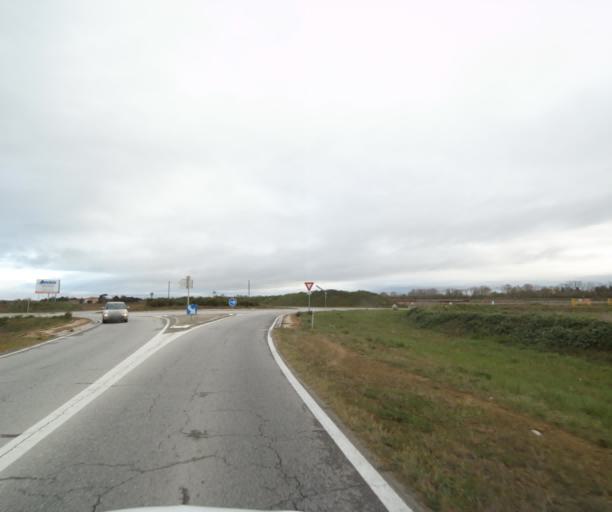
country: FR
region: Midi-Pyrenees
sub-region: Departement de l'Ariege
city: Saverdun
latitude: 43.2033
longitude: 1.6092
